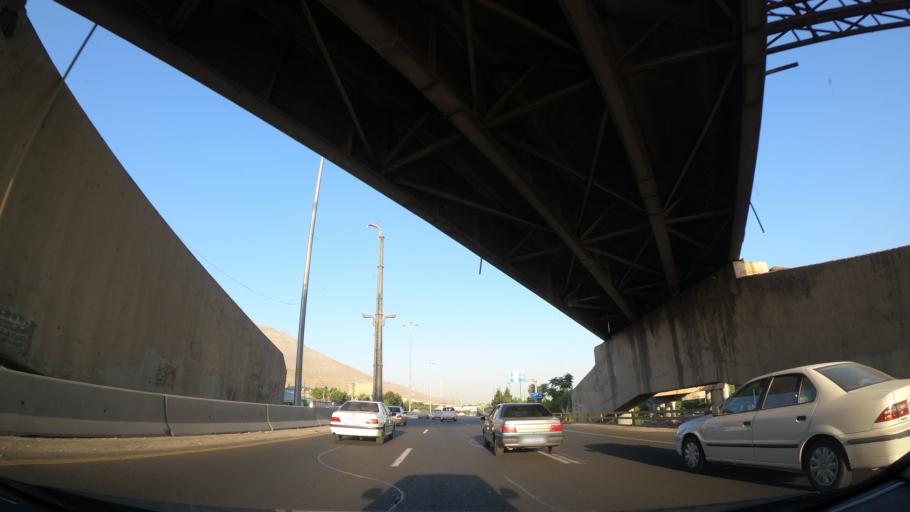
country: IR
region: Alborz
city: Karaj
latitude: 35.7883
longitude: 51.0204
